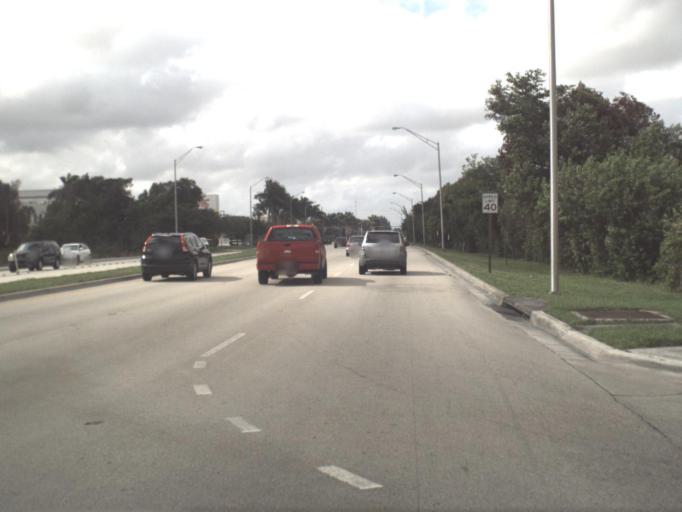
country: US
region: Florida
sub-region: Miami-Dade County
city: Doral
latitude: 25.8118
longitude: -80.3776
